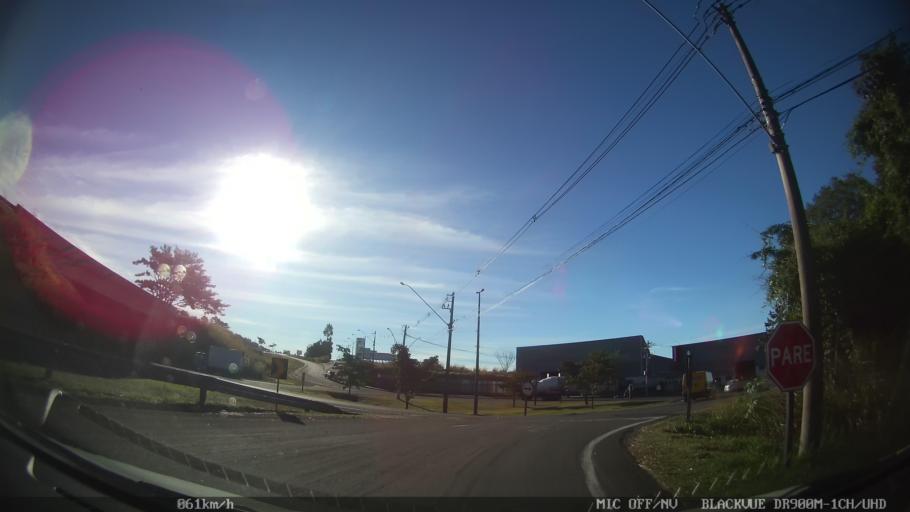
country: BR
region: Sao Paulo
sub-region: Sao Jose Do Rio Preto
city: Sao Jose do Rio Preto
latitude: -20.8707
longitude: -49.3253
